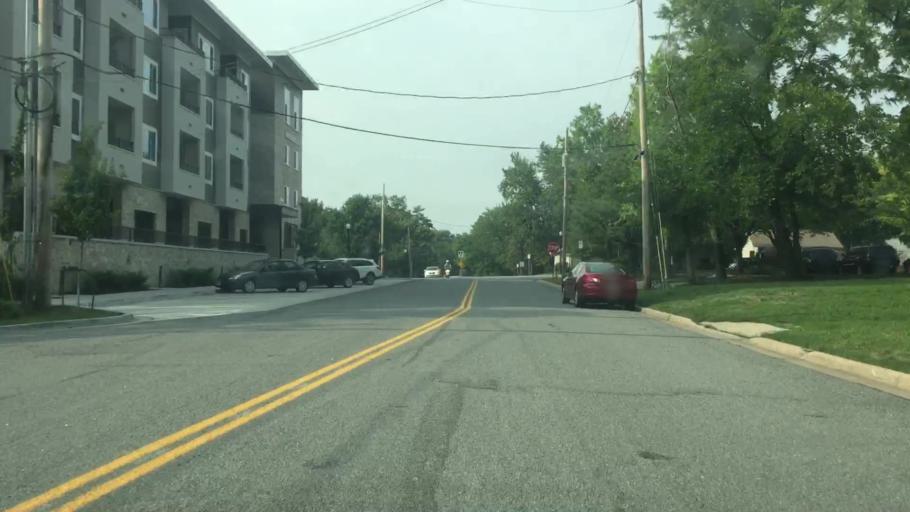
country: US
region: Kansas
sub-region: Johnson County
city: Overland Park
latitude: 38.9851
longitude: -94.6735
